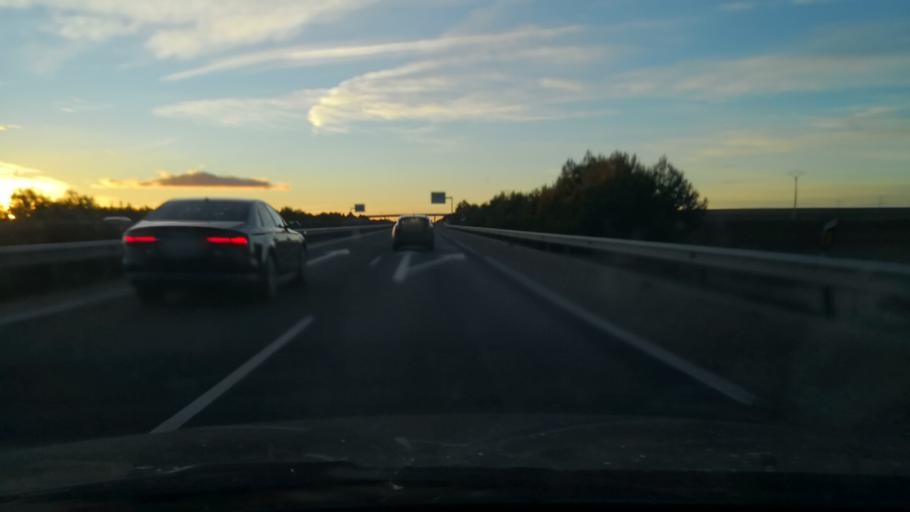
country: ES
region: Castille and Leon
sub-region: Provincia de Valladolid
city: Tordesillas
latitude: 41.5044
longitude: -5.0353
